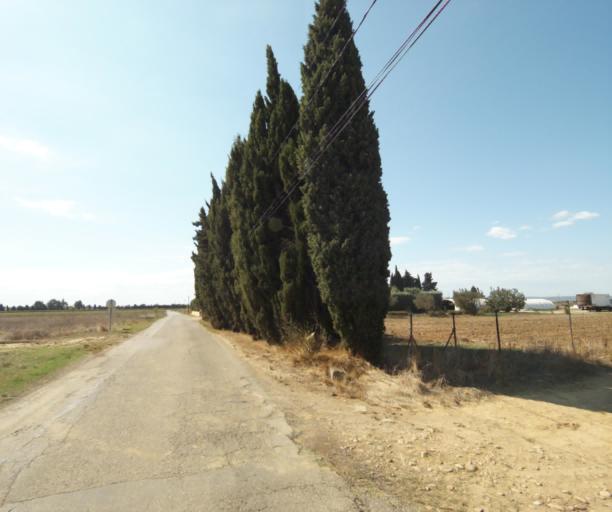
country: FR
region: Languedoc-Roussillon
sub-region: Departement du Gard
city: Manduel
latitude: 43.7995
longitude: 4.4607
